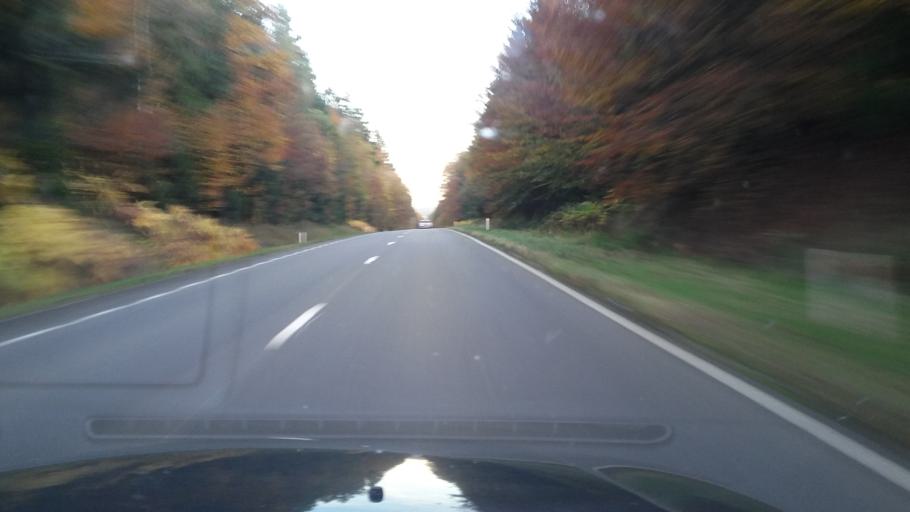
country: BE
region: Wallonia
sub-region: Province du Luxembourg
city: Herbeumont
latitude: 49.7498
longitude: 5.2097
